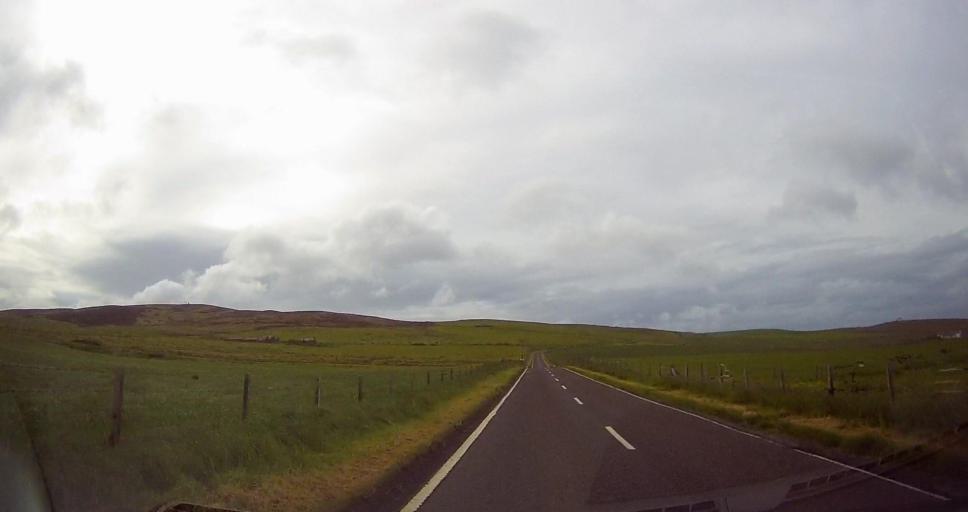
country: GB
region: Scotland
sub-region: Orkney Islands
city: Stromness
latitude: 58.9300
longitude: -3.2057
